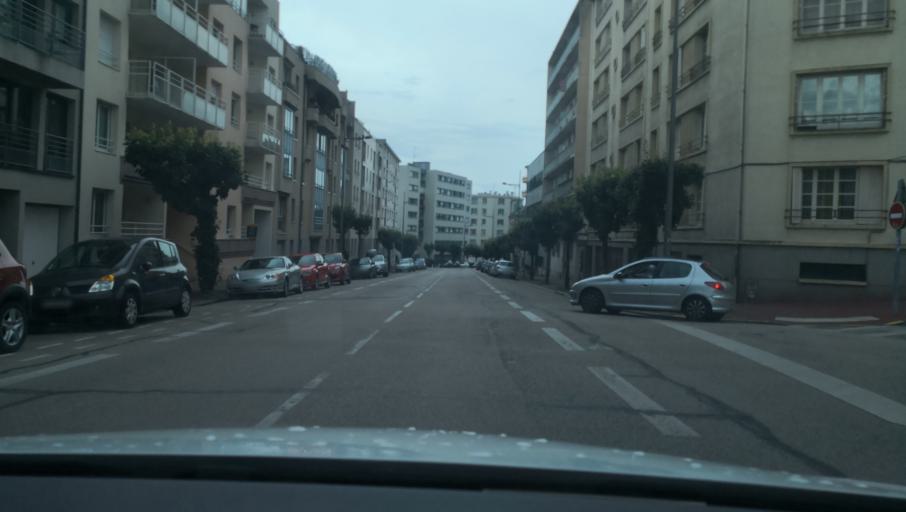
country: FR
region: Limousin
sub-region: Departement de la Haute-Vienne
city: Limoges
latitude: 45.8382
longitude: 1.2635
